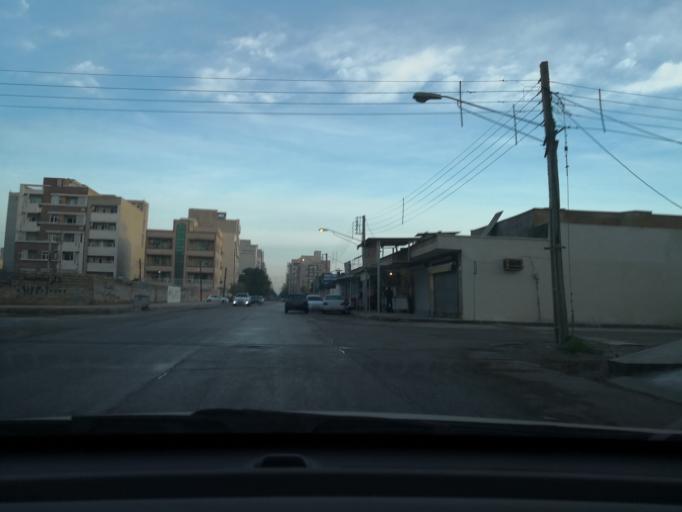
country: IR
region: Khuzestan
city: Ahvaz
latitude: 31.3511
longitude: 48.6785
